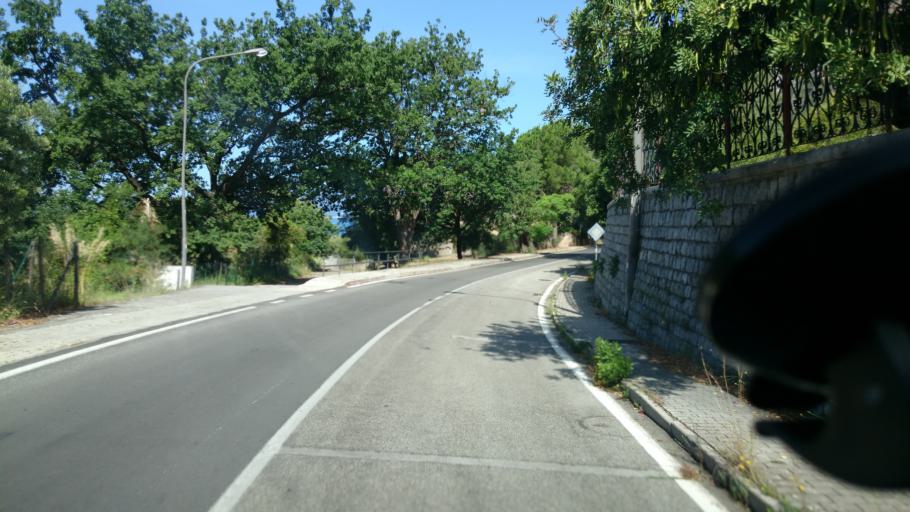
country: IT
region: Basilicate
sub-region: Provincia di Potenza
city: Maratea
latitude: 40.0357
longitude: 15.6728
